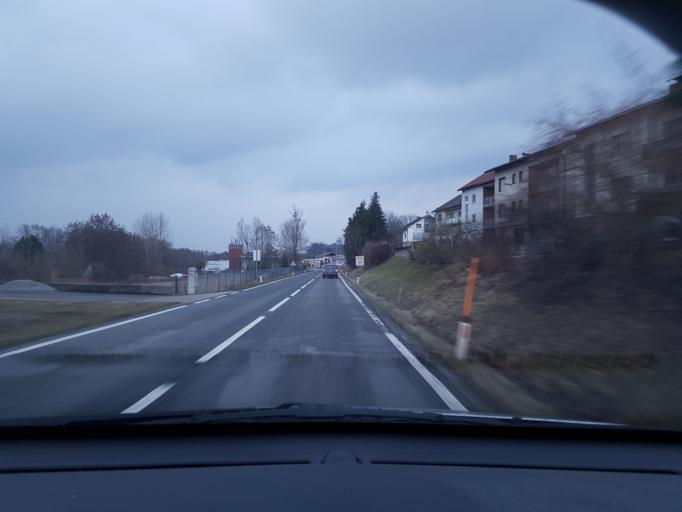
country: AT
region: Upper Austria
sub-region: Politischer Bezirk Linz-Land
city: Sankt Florian
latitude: 48.1621
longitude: 14.3372
